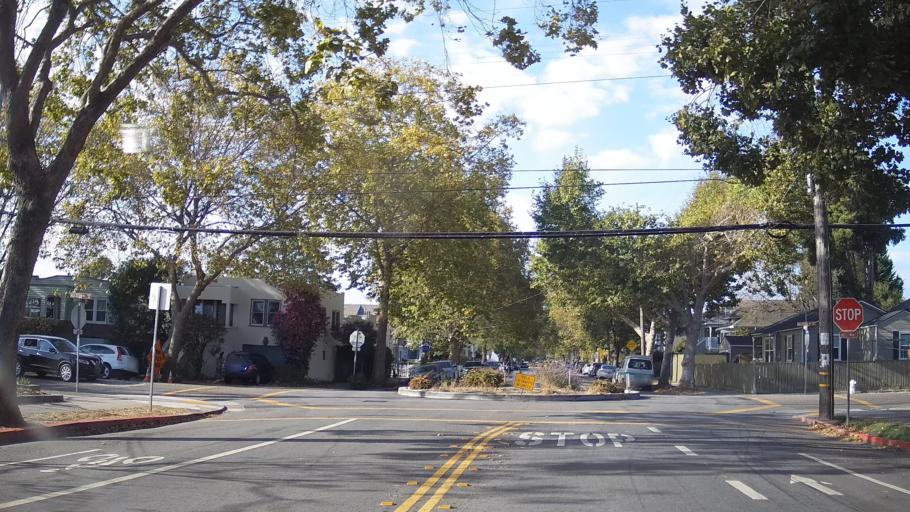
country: US
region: California
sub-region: Alameda County
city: Berkeley
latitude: 37.8657
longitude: -122.2935
